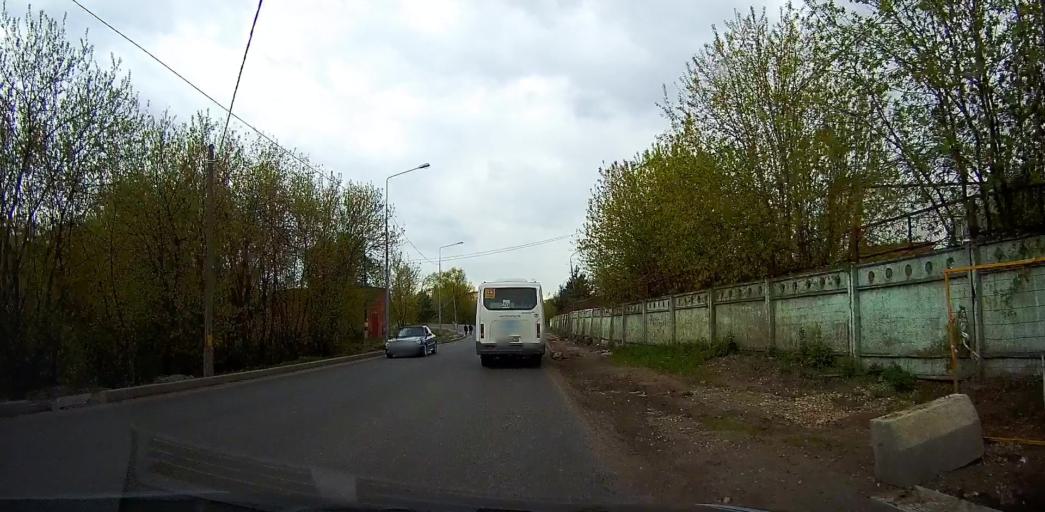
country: RU
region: Moskovskaya
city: Pavlovskiy Posad
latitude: 55.7819
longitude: 38.6892
